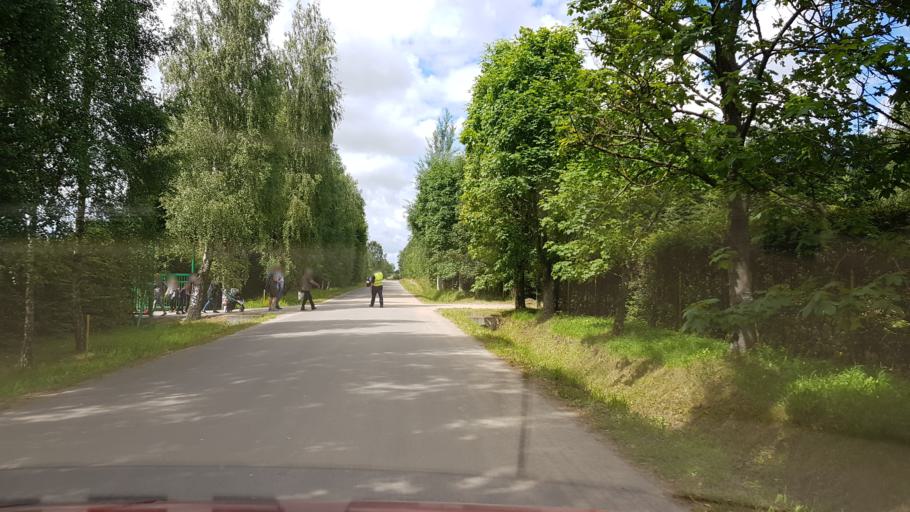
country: PL
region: West Pomeranian Voivodeship
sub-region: Powiat bialogardzki
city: Karlino
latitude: 54.1658
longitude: 15.9245
